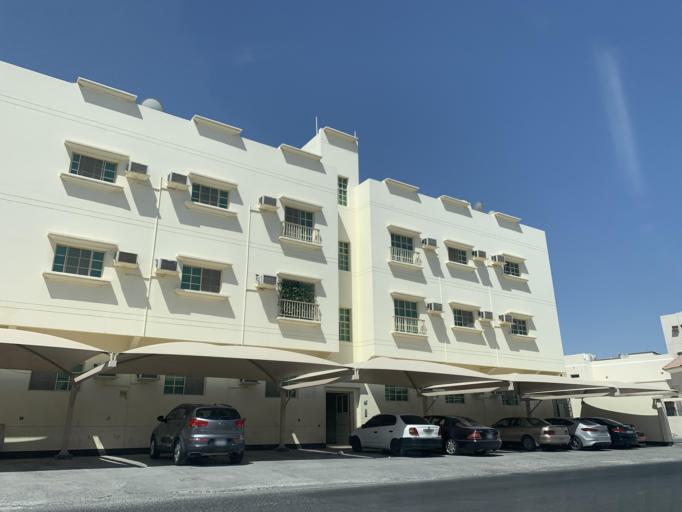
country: BH
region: Northern
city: Ar Rifa'
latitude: 26.1347
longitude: 50.5780
